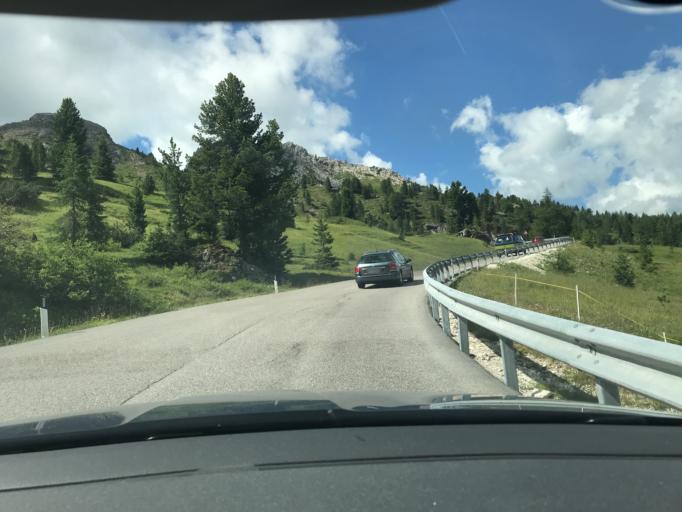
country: IT
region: Veneto
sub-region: Provincia di Belluno
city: Livinallongo del Col di Lana
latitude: 46.5359
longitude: 11.9854
